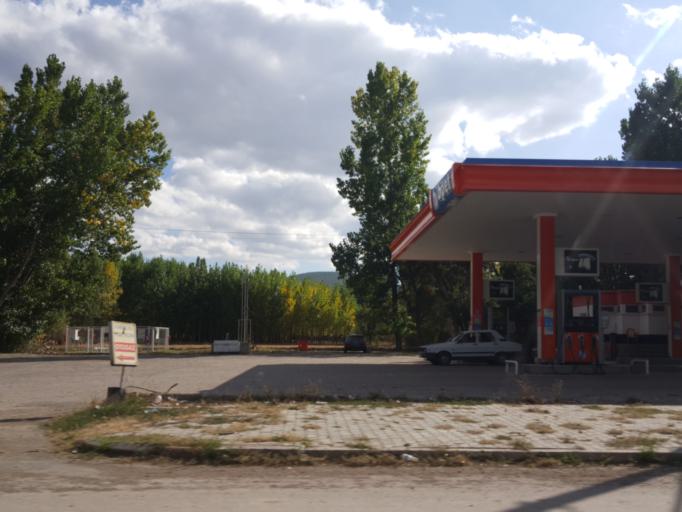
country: TR
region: Tokat
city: Yesilyurt
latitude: 40.0081
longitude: 36.2037
